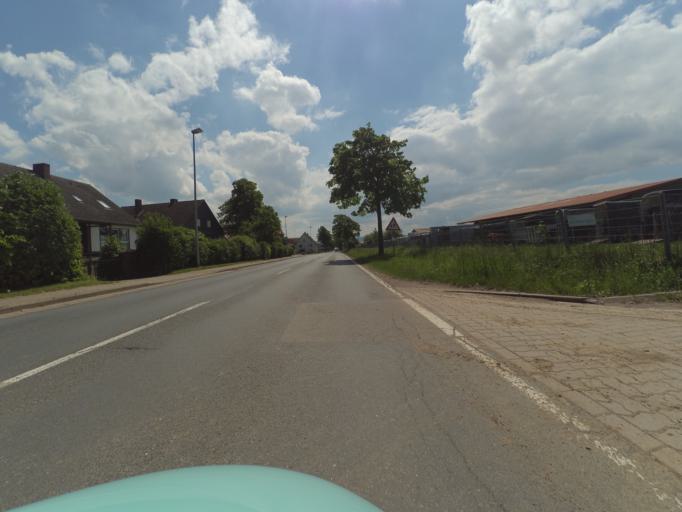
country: DE
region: Lower Saxony
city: Hohenhameln
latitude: 52.2027
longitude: 10.0344
